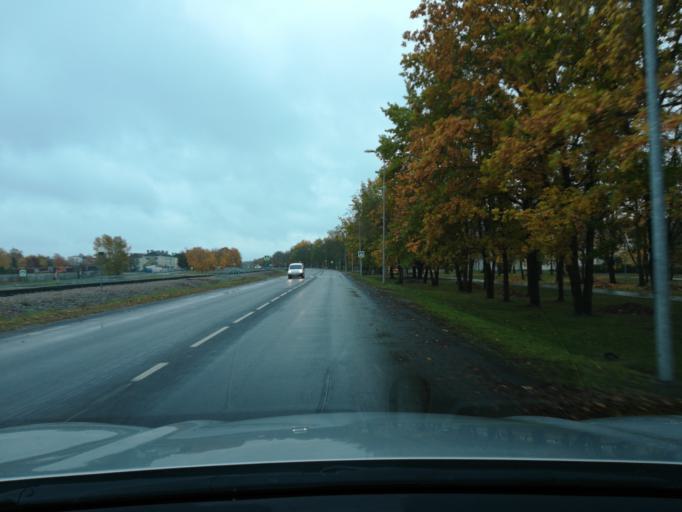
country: EE
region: Ida-Virumaa
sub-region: Johvi vald
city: Johvi
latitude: 59.3261
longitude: 27.4193
